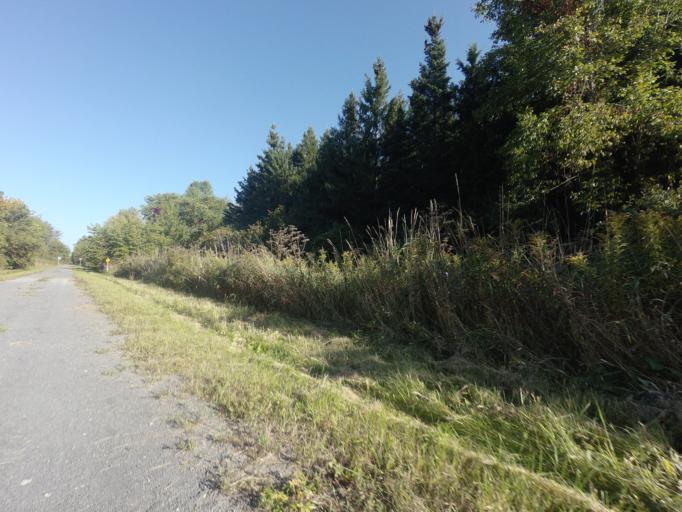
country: CA
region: Ontario
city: Hawkesbury
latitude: 45.5362
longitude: -74.6343
